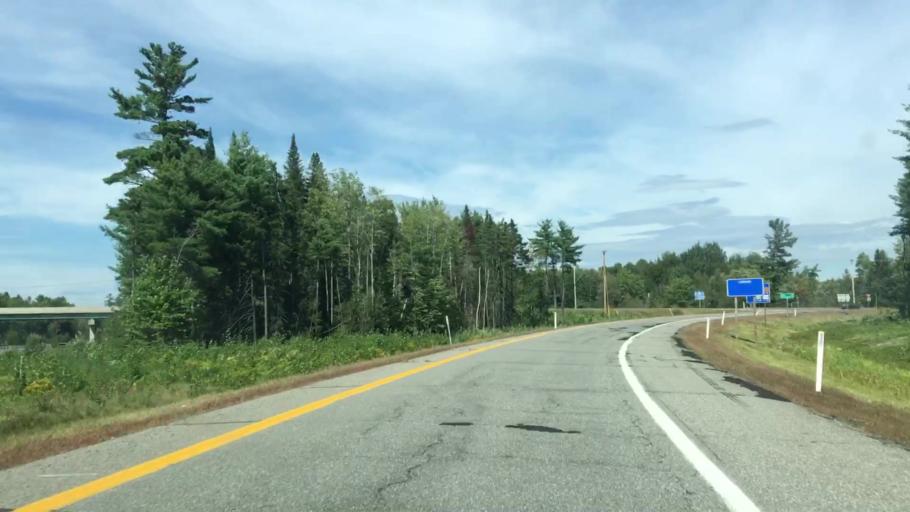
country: US
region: Maine
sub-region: Penobscot County
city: Lincoln
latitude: 45.3738
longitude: -68.6042
